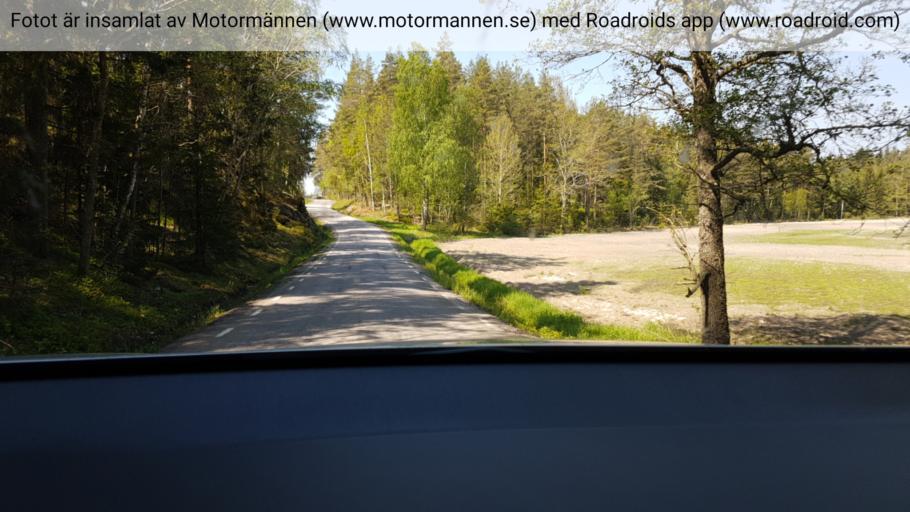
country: SE
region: Kalmar
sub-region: Vasterviks Kommun
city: Gamleby
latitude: 57.8700
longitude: 16.4696
